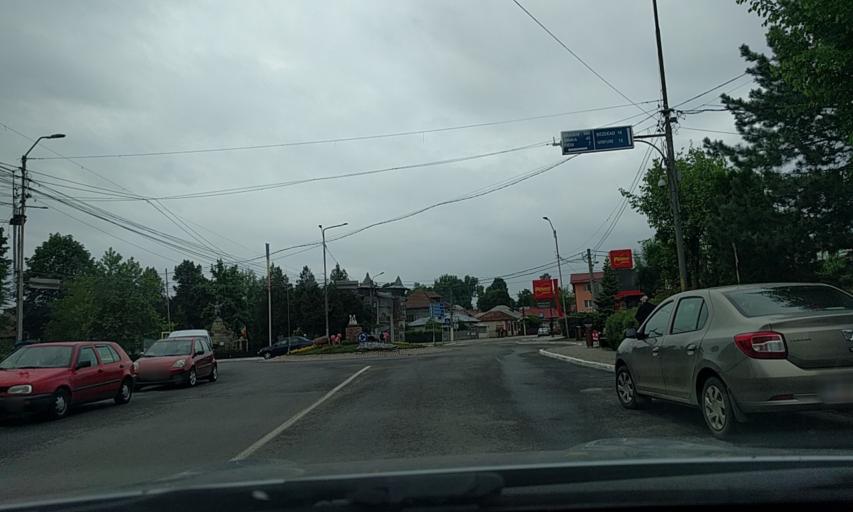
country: RO
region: Dambovita
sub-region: Oras Pucioasa
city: Pucioasa
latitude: 45.0776
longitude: 25.4338
